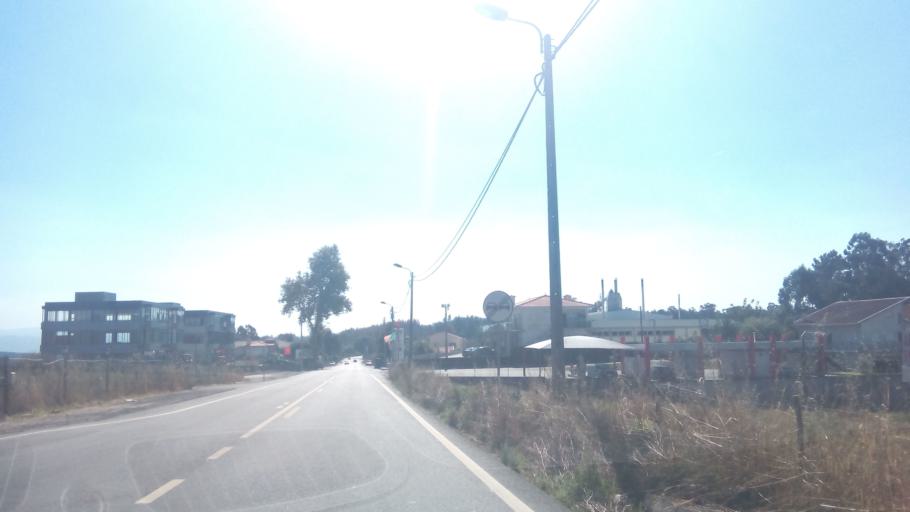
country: PT
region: Porto
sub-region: Amarante
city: Figueiro
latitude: 41.2709
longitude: -8.2084
